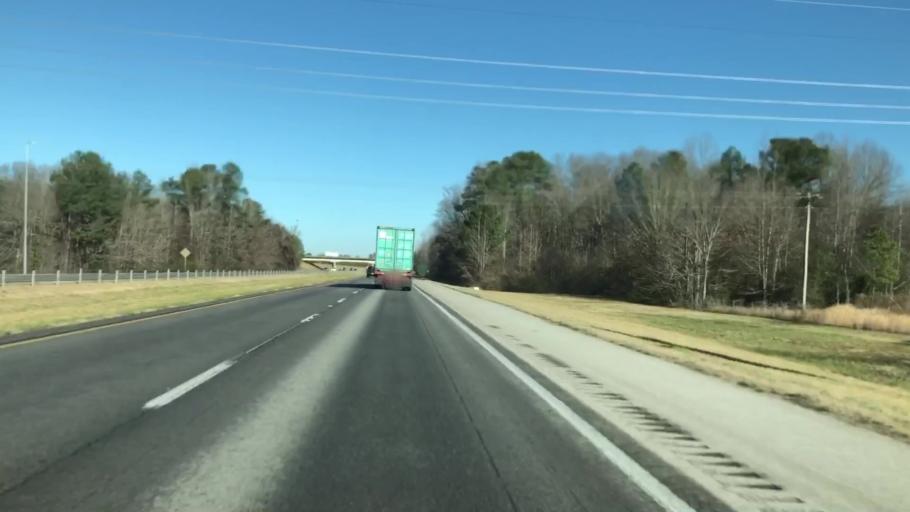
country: US
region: Alabama
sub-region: Limestone County
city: Athens
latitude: 34.8237
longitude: -86.9387
